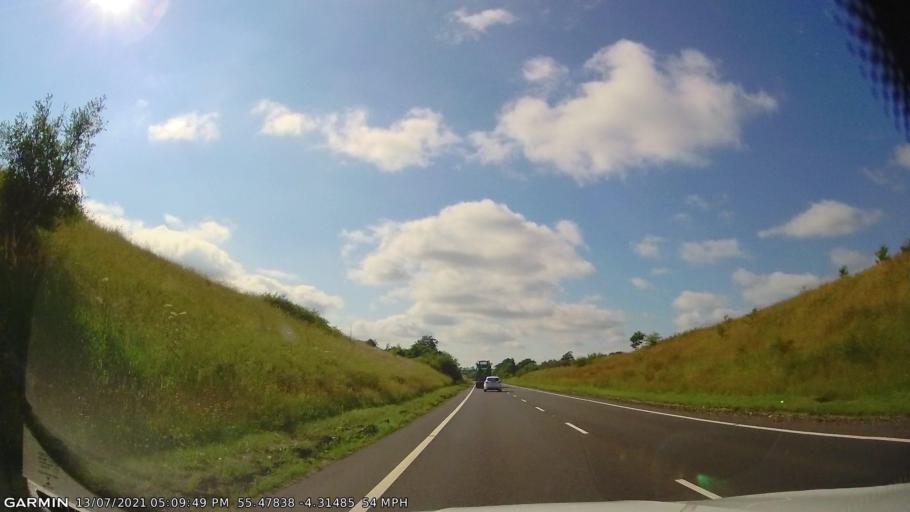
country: GB
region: Scotland
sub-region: East Ayrshire
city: Auchinleck
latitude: 55.4780
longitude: -4.3143
